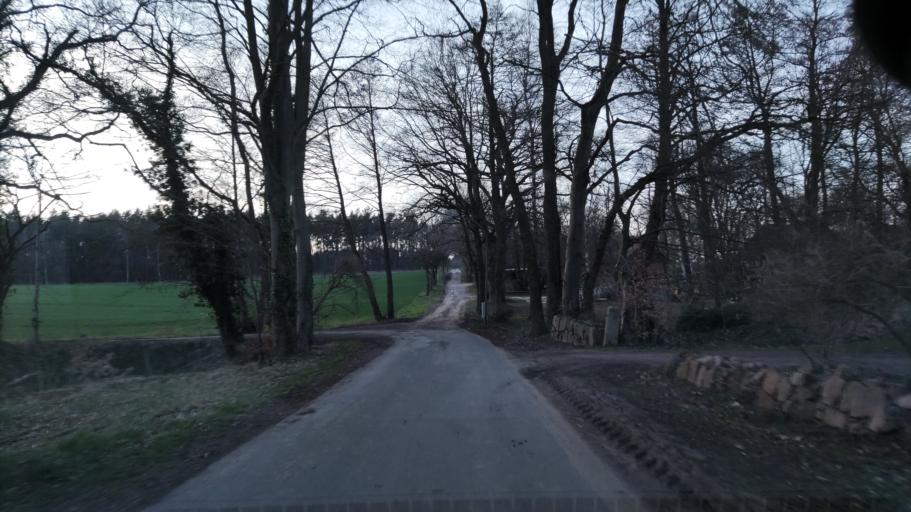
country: DE
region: Lower Saxony
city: Thomasburg
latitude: 53.2082
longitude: 10.6983
